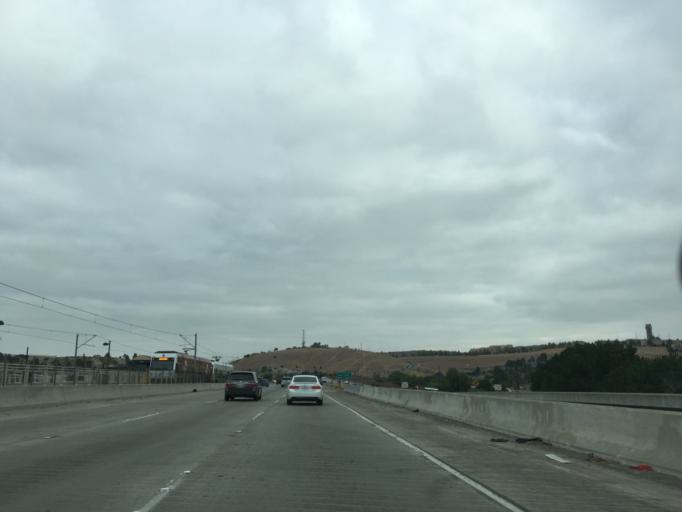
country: US
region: California
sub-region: Santa Clara County
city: Seven Trees
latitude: 37.2743
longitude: -121.8629
